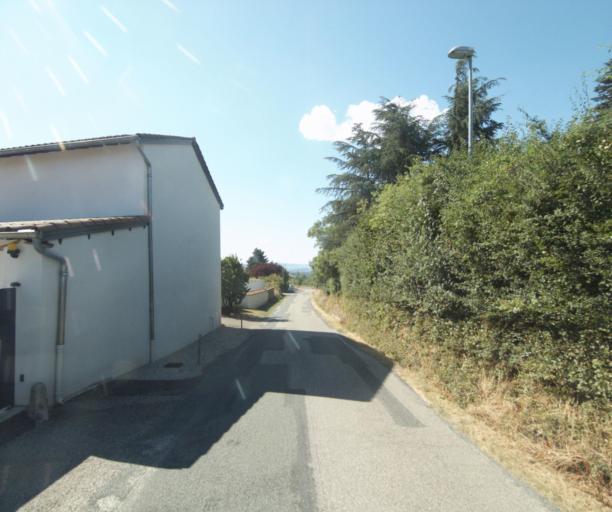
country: FR
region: Rhone-Alpes
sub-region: Departement du Rhone
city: La Tour-de-Salvagny
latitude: 45.8325
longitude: 4.7043
